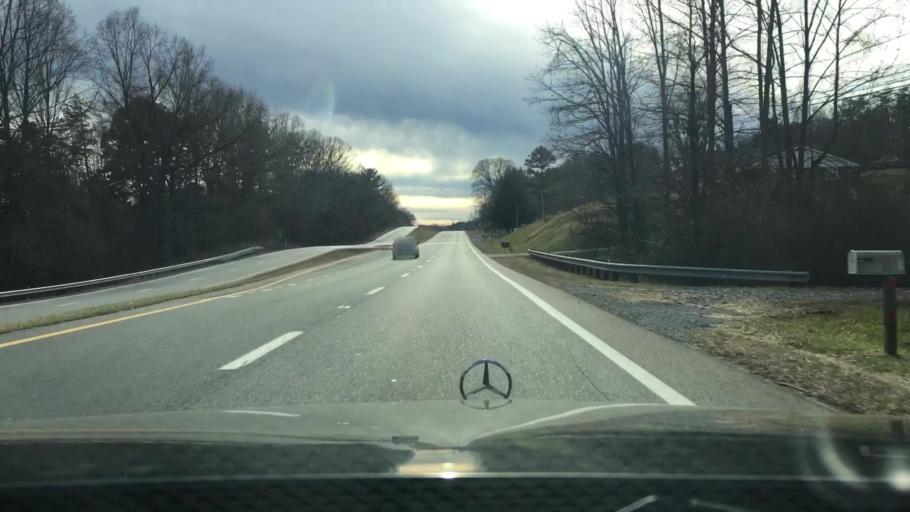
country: US
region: Virginia
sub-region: Pittsylvania County
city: Motley
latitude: 37.0550
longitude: -79.3529
